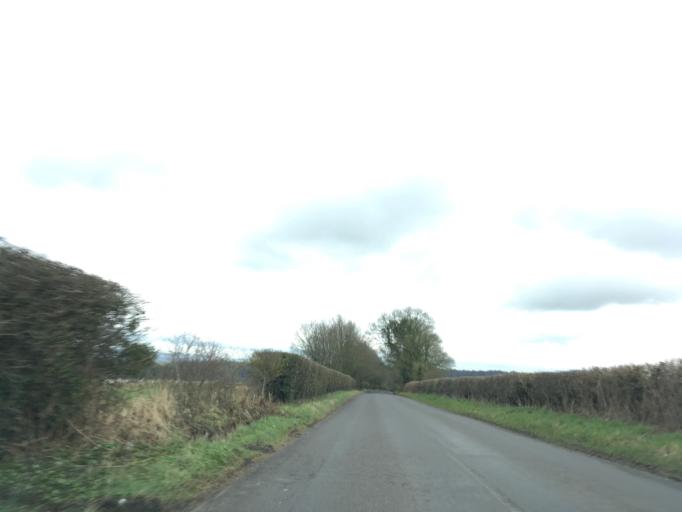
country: GB
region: England
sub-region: Wiltshire
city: Chilton Foliat
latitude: 51.4420
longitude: -1.5370
